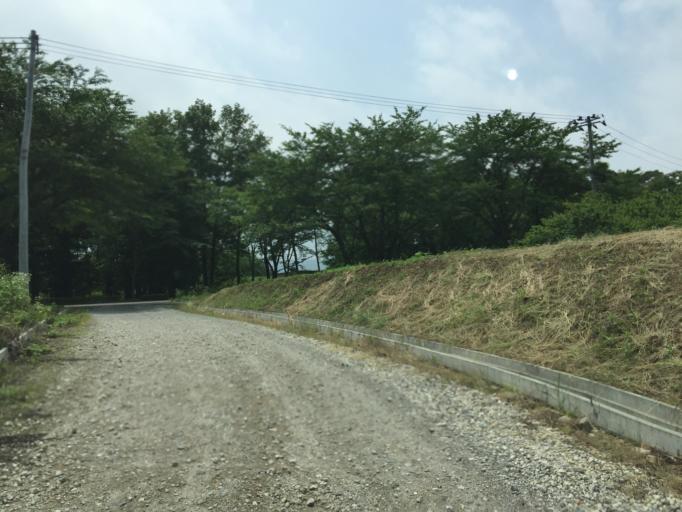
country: JP
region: Fukushima
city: Fukushima-shi
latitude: 37.7342
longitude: 140.3788
